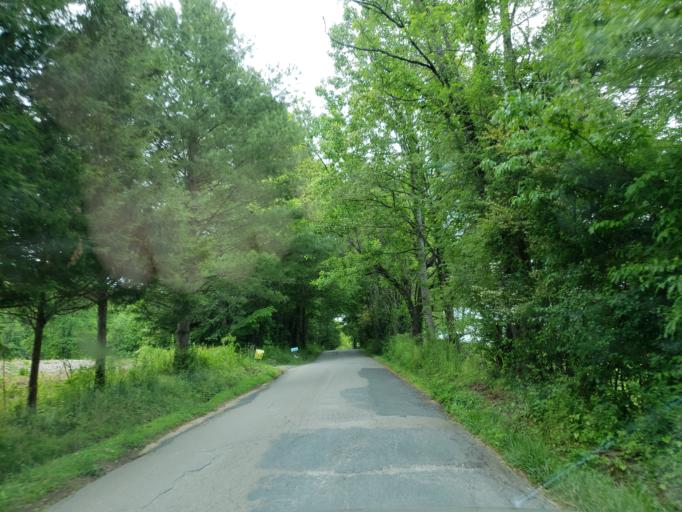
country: US
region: Georgia
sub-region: Fannin County
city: Blue Ridge
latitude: 34.8308
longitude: -84.4081
